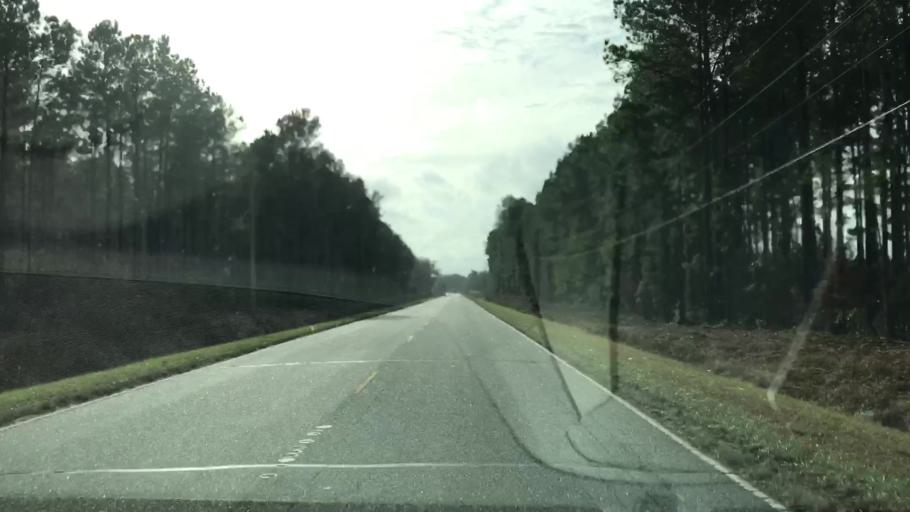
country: US
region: South Carolina
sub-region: Williamsburg County
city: Andrews
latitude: 33.3653
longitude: -79.6457
